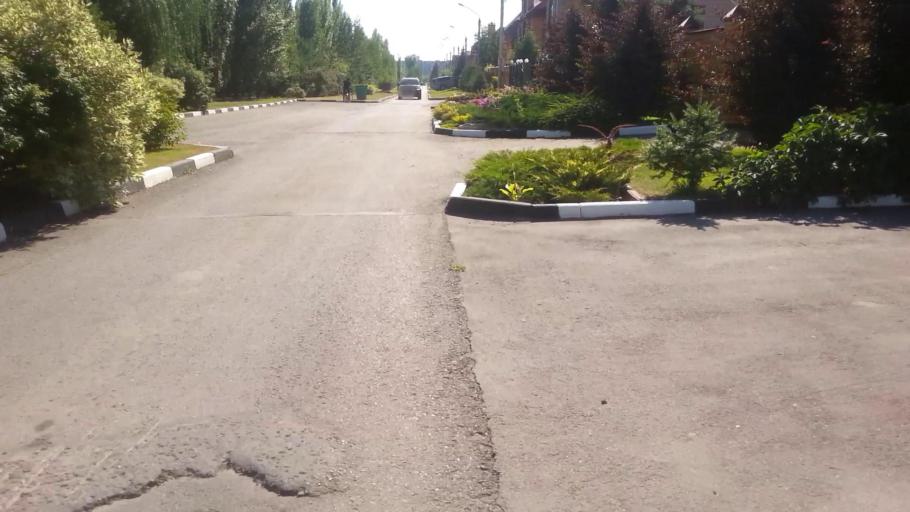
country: RU
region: Altai Krai
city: Novosilikatnyy
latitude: 53.3557
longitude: 83.6571
